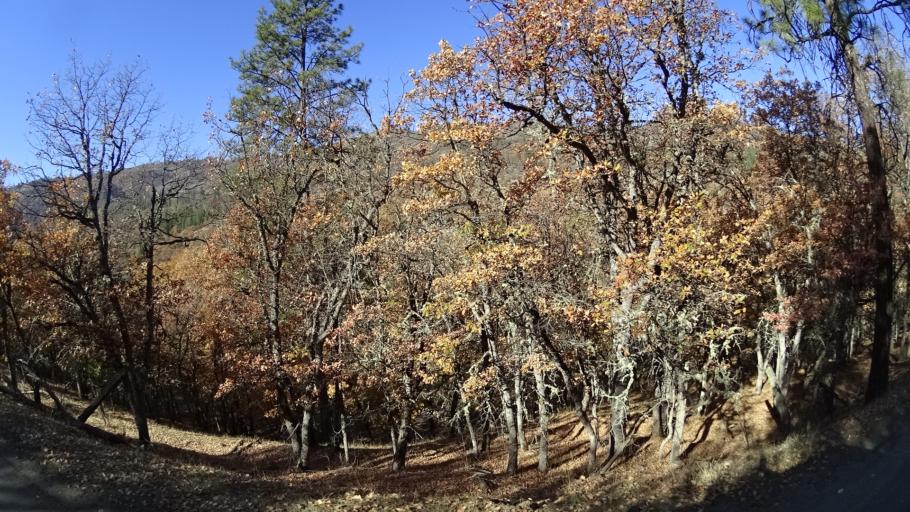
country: US
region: California
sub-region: Siskiyou County
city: Yreka
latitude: 41.8584
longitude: -122.8255
